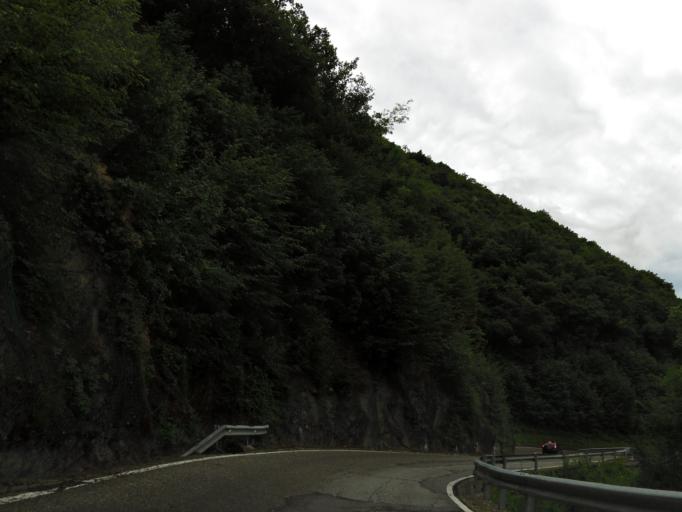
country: IT
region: Trentino-Alto Adige
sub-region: Bolzano
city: Collalbo
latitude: 46.5013
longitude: 11.4604
